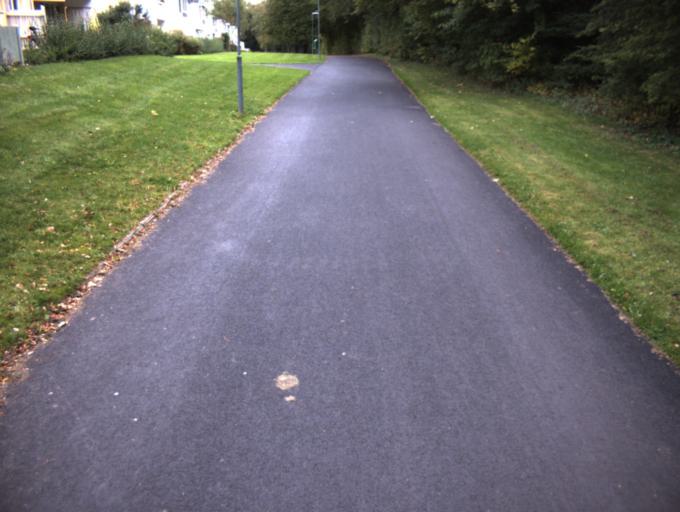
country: SE
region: Skane
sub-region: Helsingborg
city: Odakra
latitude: 56.0649
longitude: 12.7316
